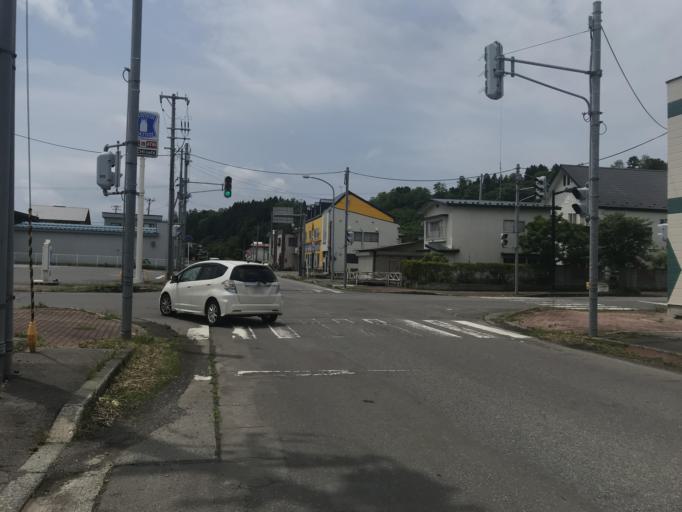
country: JP
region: Aomori
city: Shimokizukuri
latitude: 40.7764
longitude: 140.2190
